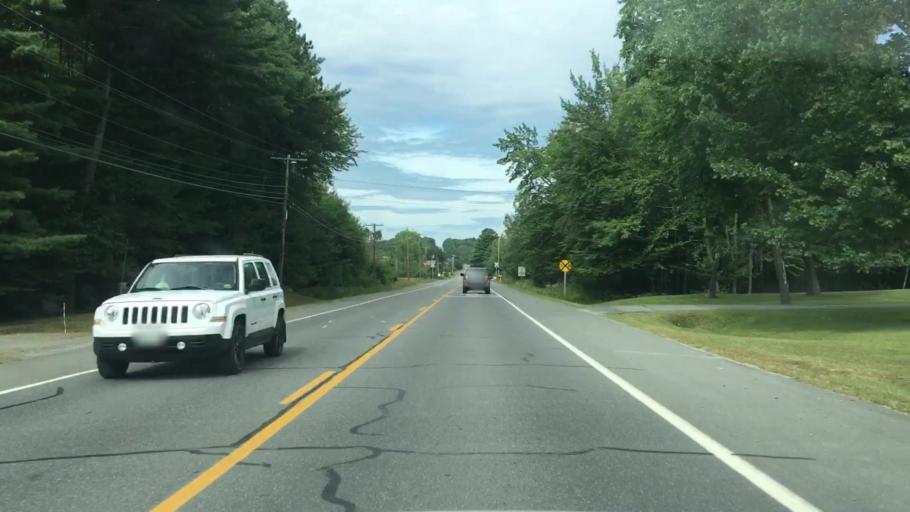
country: US
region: Maine
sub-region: Piscataquis County
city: Milo
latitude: 45.2681
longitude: -68.9960
